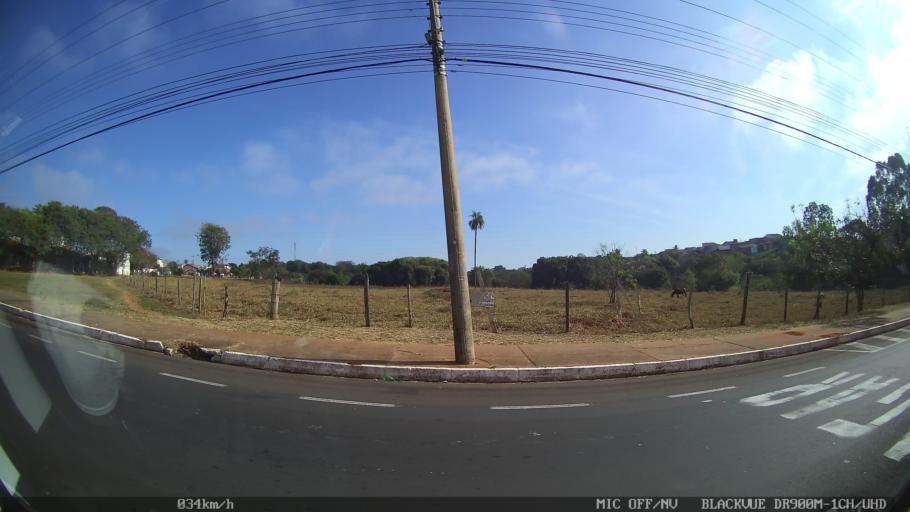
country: BR
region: Sao Paulo
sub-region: Sao Jose Do Rio Preto
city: Sao Jose do Rio Preto
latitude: -20.7964
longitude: -49.4273
